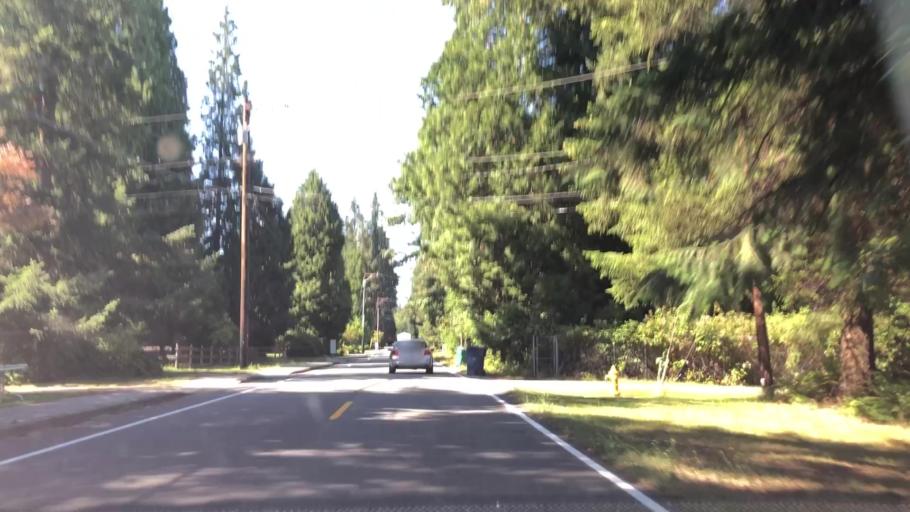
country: US
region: Washington
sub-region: King County
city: Woodinville
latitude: 47.7869
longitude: -122.1675
